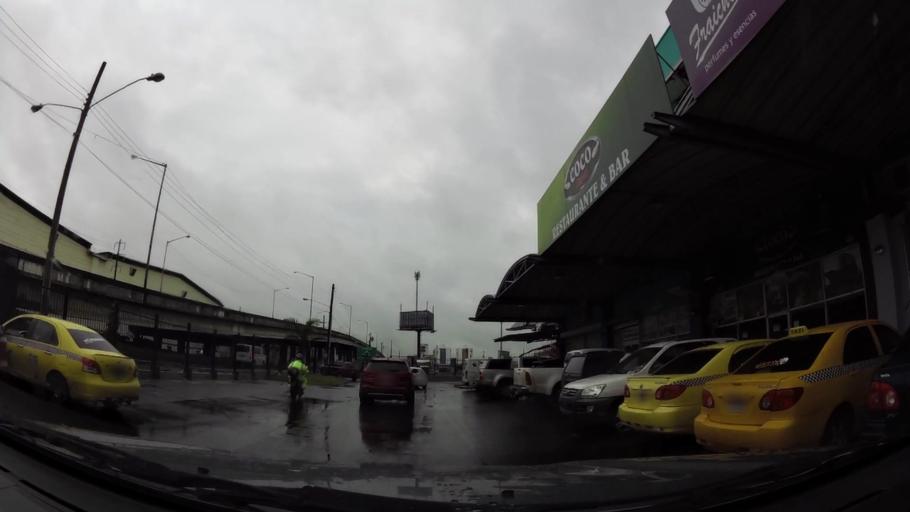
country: PA
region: Colon
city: Arco Iris
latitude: 9.3389
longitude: -79.8822
